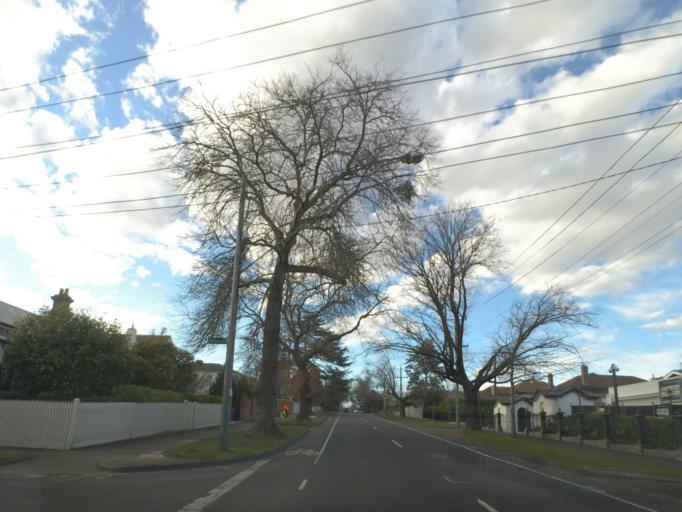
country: AU
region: Victoria
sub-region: Boroondara
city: Canterbury
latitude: -37.8216
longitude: 145.0797
